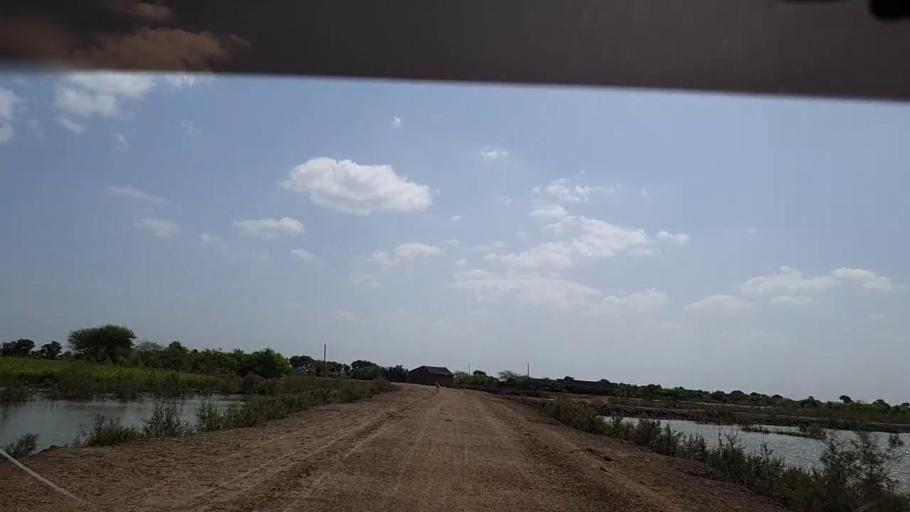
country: PK
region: Sindh
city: Badin
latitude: 24.5673
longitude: 68.8044
